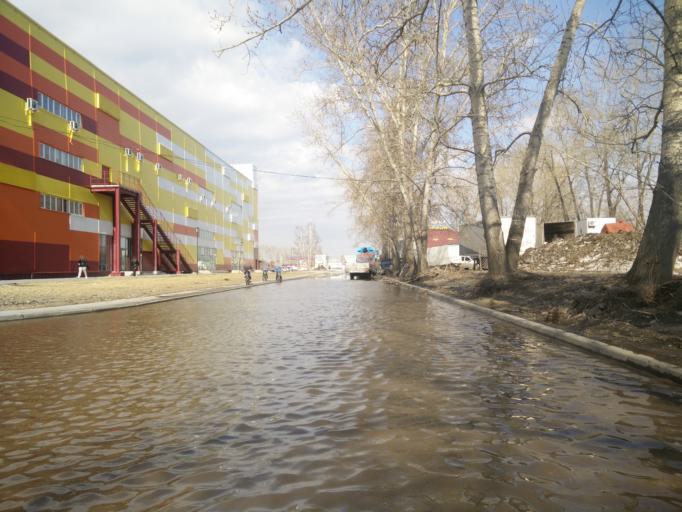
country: RU
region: Novosibirsk
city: Berdsk
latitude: 54.7644
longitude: 83.0802
